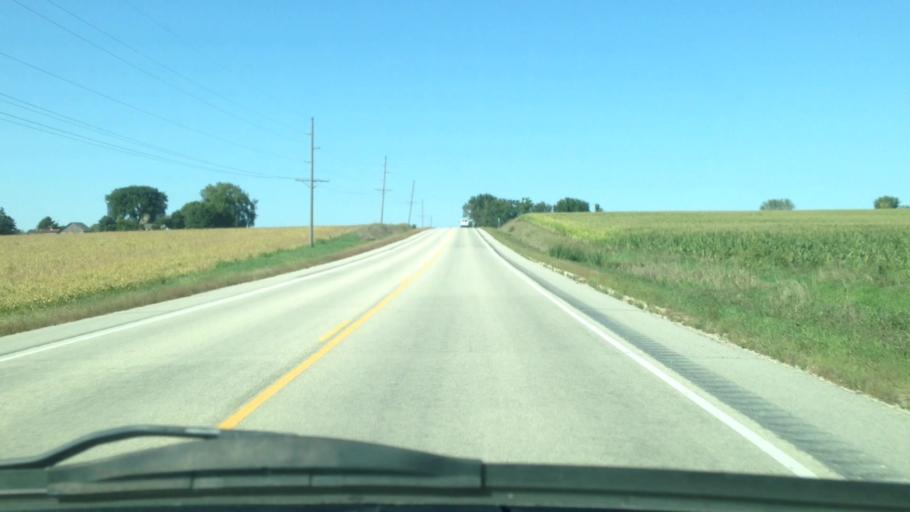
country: US
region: Minnesota
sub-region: Fillmore County
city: Rushford
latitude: 43.9045
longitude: -91.7401
